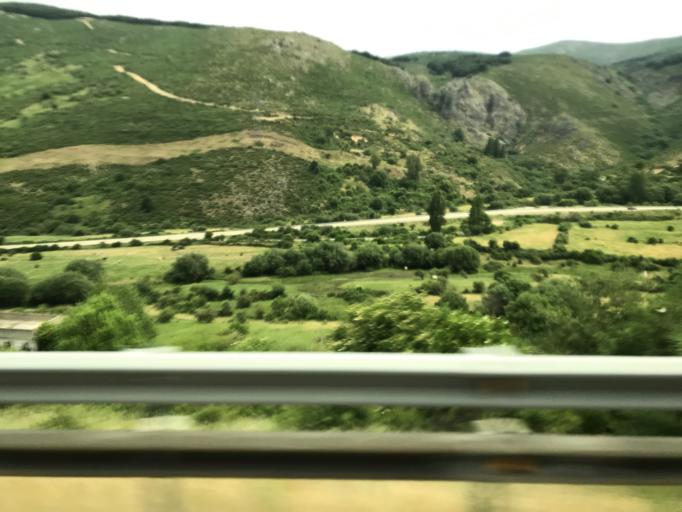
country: ES
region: Madrid
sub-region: Provincia de Madrid
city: Somosierra
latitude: 41.1448
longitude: -3.5823
